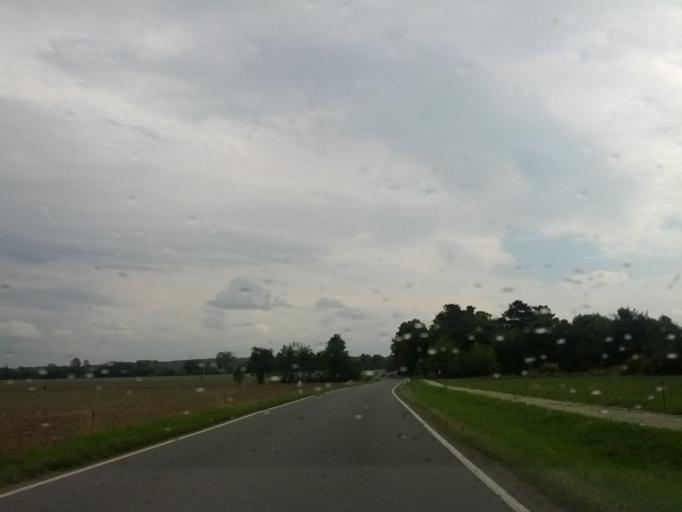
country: DE
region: Thuringia
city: Ernstroda
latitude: 50.8641
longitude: 10.6301
